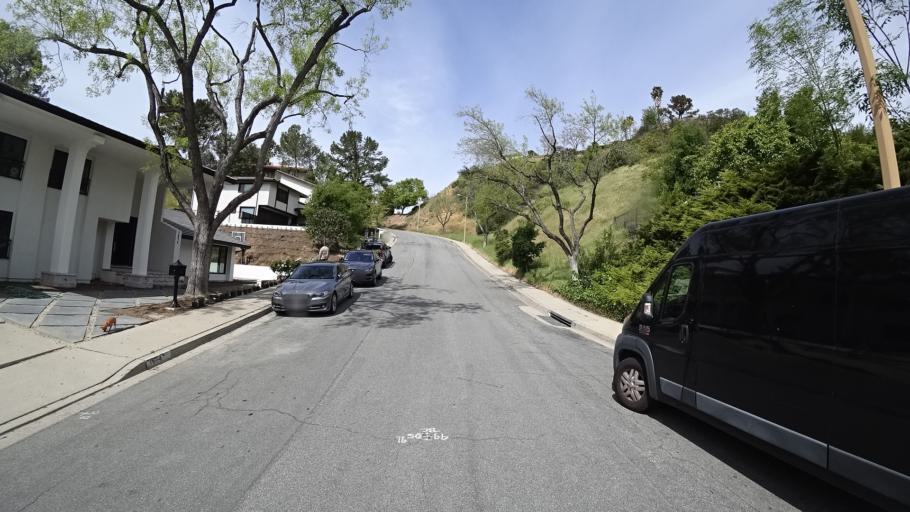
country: US
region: California
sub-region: Ventura County
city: Thousand Oaks
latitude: 34.1522
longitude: -118.8478
